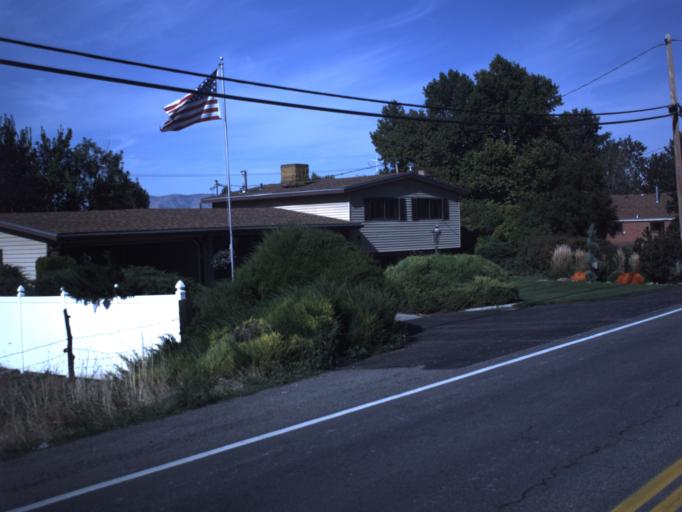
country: US
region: Utah
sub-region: Utah County
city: Orem
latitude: 40.2510
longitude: -111.7045
